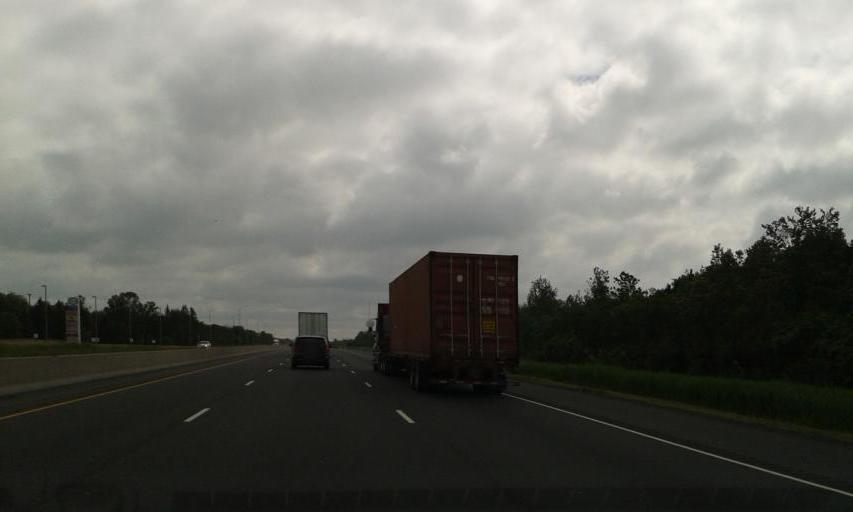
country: CA
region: Ontario
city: Oshawa
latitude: 43.9194
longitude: -78.5425
